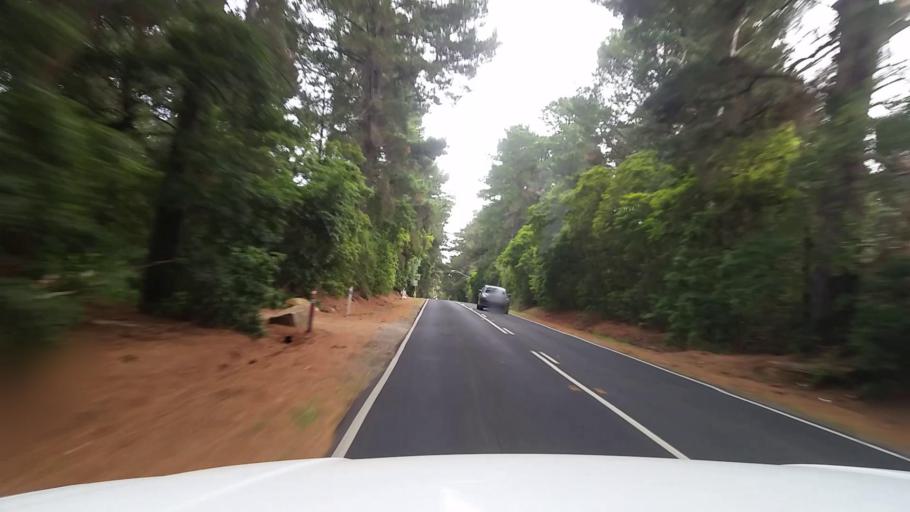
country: AU
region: Victoria
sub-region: Mornington Peninsula
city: Balnarring
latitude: -38.3683
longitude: 145.1215
